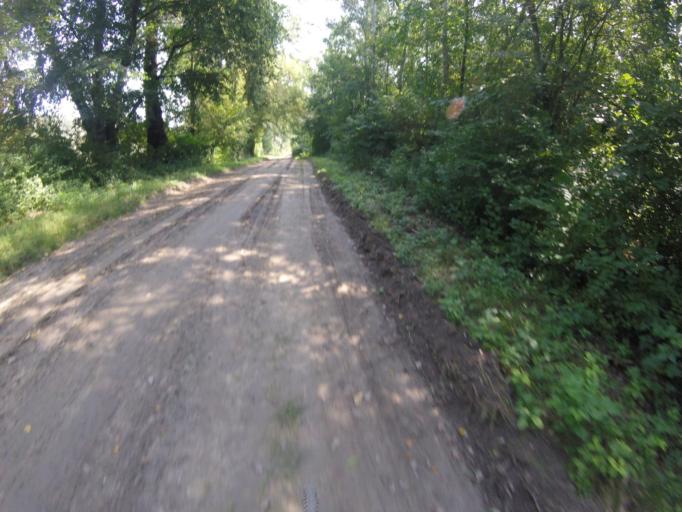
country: HU
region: Bacs-Kiskun
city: Baja
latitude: 46.1964
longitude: 18.9101
